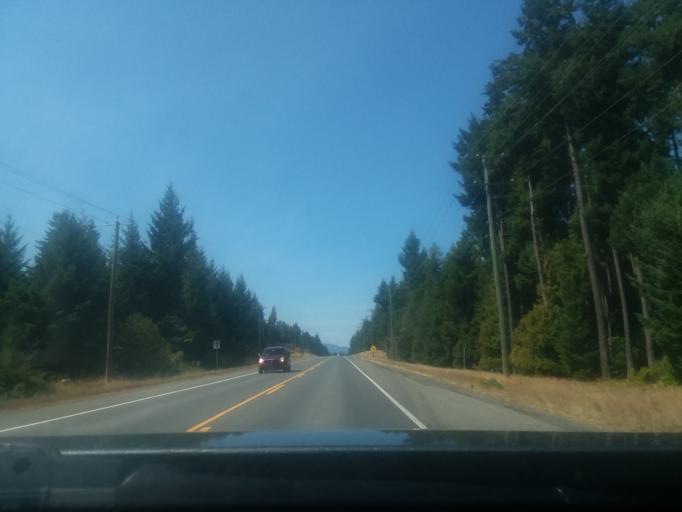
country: CA
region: British Columbia
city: Courtenay
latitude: 49.7152
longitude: -124.9380
